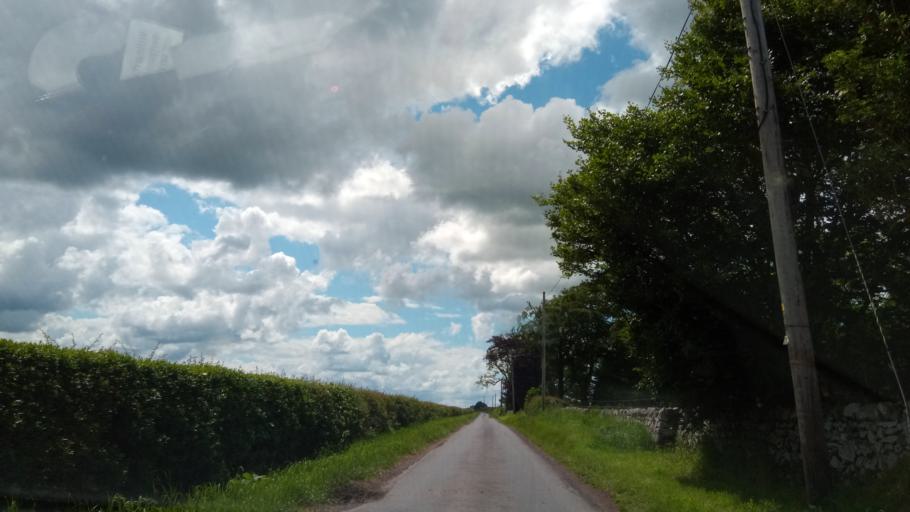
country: GB
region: Scotland
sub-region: The Scottish Borders
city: Coldstream
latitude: 55.5833
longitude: -2.3068
